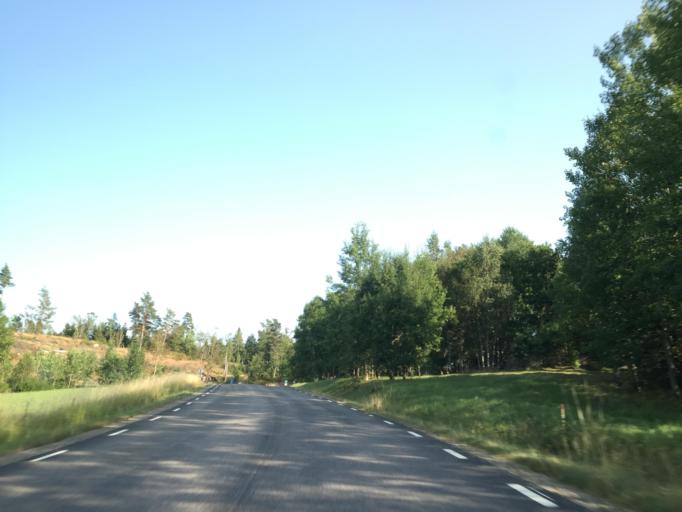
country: SE
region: Vaestra Goetaland
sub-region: Trollhattan
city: Trollhattan
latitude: 58.2728
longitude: 12.2480
